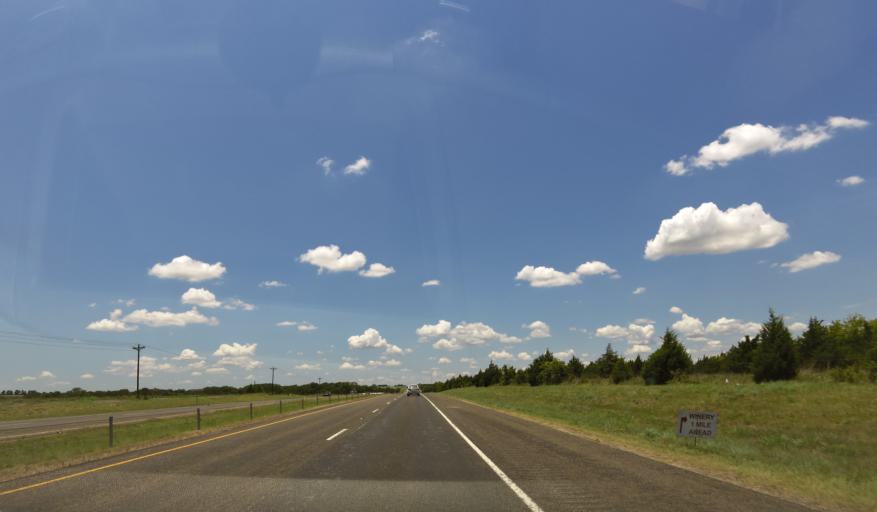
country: US
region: Texas
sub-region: Washington County
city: Brenham
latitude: 30.1911
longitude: -96.5351
